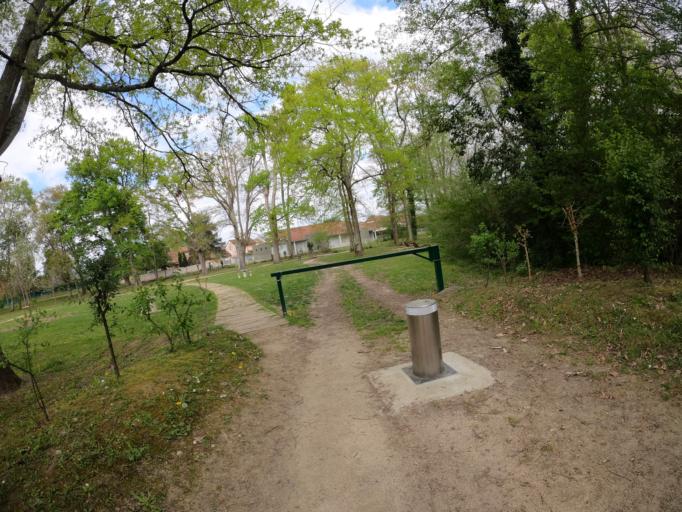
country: FR
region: Aquitaine
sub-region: Departement des Pyrenees-Atlantiques
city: Lons
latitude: 43.3301
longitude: -0.3912
